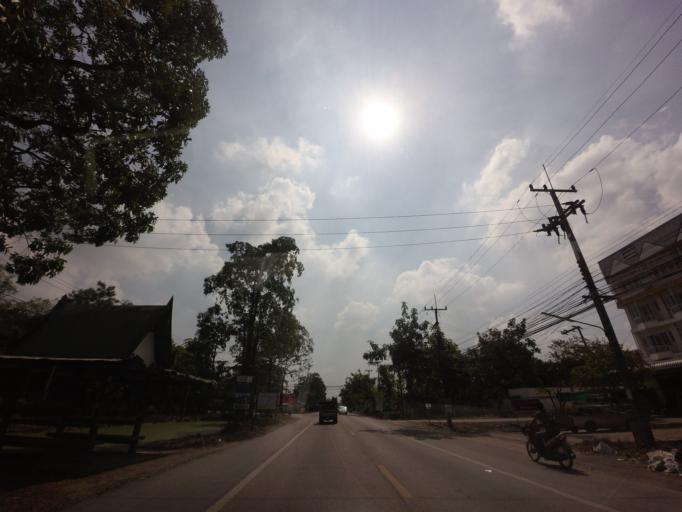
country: TH
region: Nakhon Pathom
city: Sam Phran
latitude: 13.7533
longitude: 100.2304
